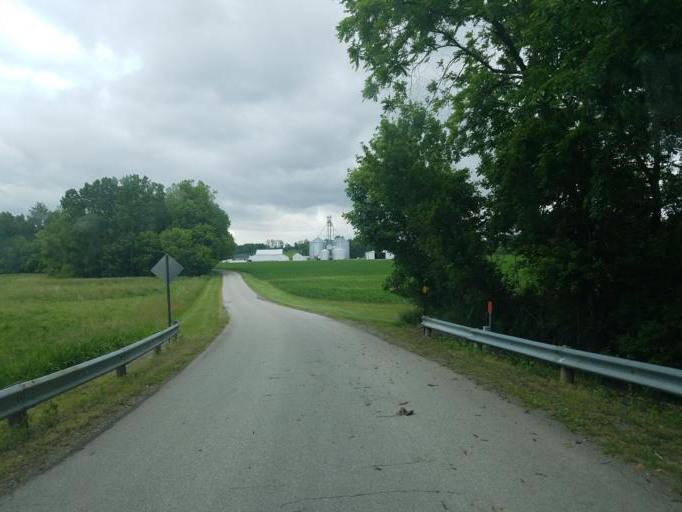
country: US
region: Ohio
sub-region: Wyandot County
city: Upper Sandusky
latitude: 40.7546
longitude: -83.2202
